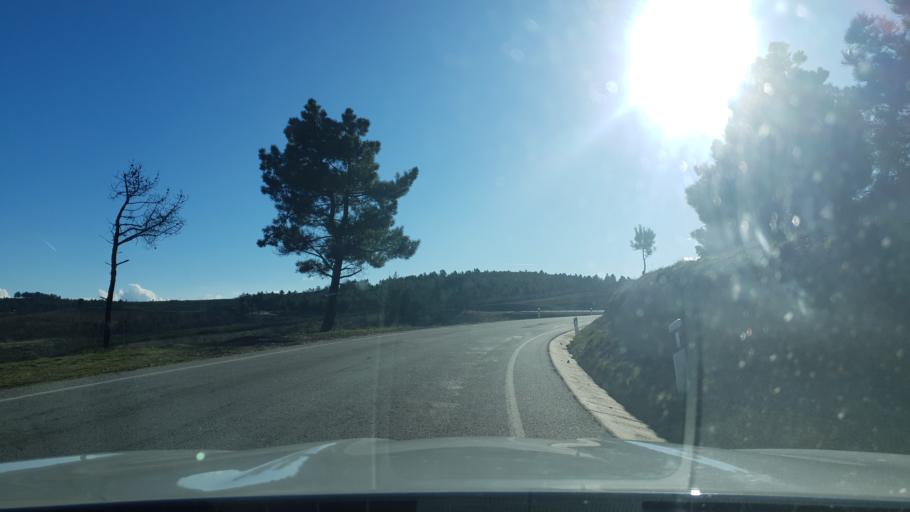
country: PT
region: Braganca
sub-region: Freixo de Espada A Cinta
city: Freixo de Espada a Cinta
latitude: 41.1649
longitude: -6.7977
